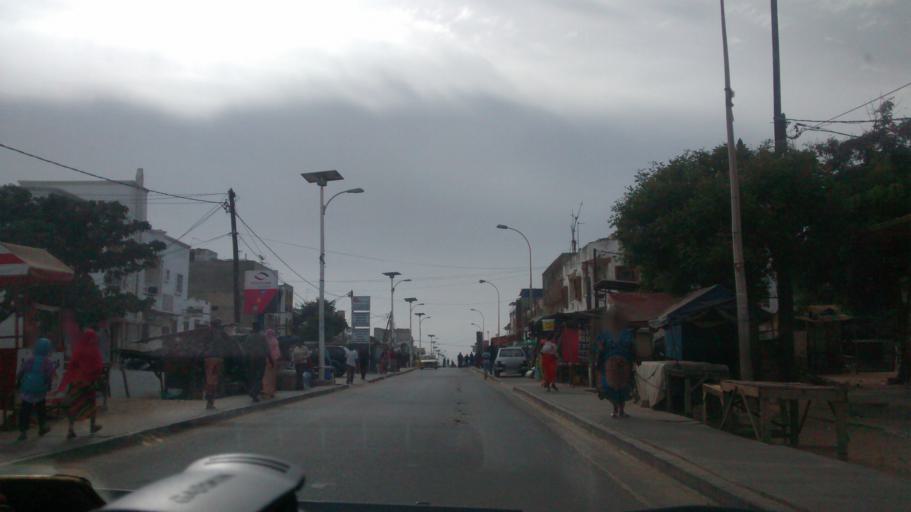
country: SN
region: Dakar
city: Pikine
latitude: 14.7820
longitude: -17.3816
